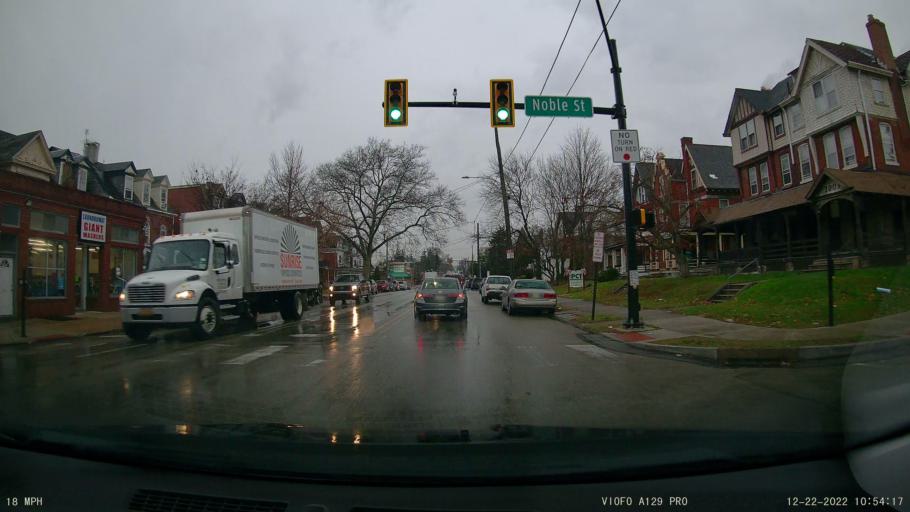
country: US
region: Pennsylvania
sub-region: Montgomery County
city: Norristown
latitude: 40.1204
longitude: -75.3569
